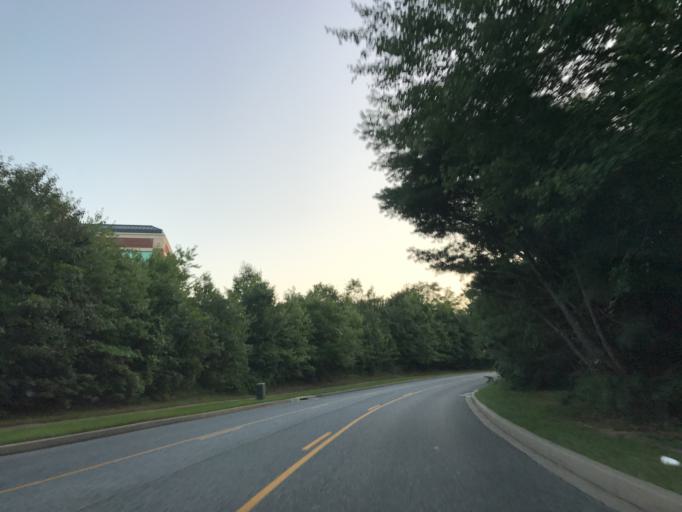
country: US
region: Maryland
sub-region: Harford County
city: Bel Air South
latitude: 39.4701
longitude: -76.3026
